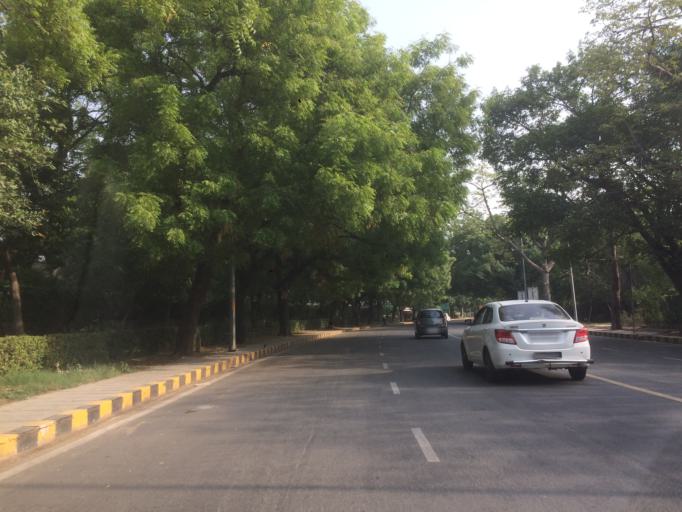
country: IN
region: NCT
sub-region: New Delhi
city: New Delhi
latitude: 28.5872
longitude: 77.1827
